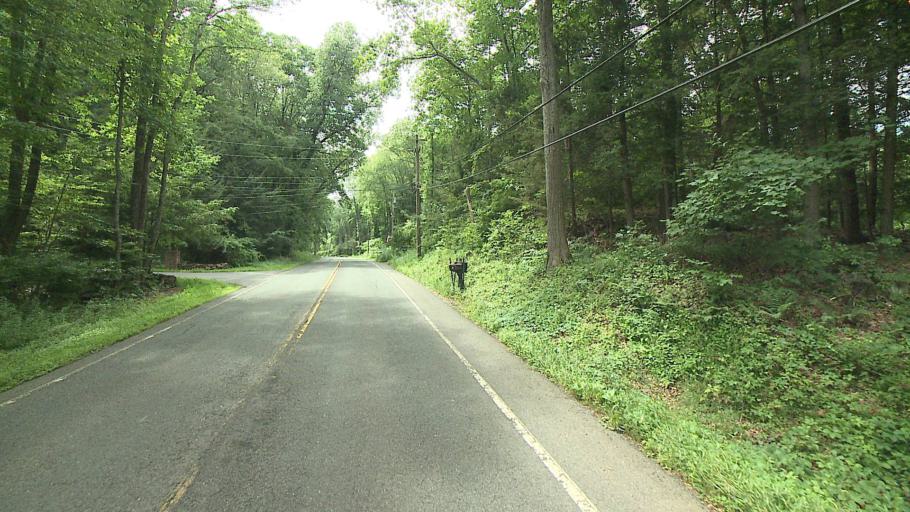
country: US
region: Connecticut
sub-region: Fairfield County
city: Sherman
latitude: 41.6440
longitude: -73.5027
